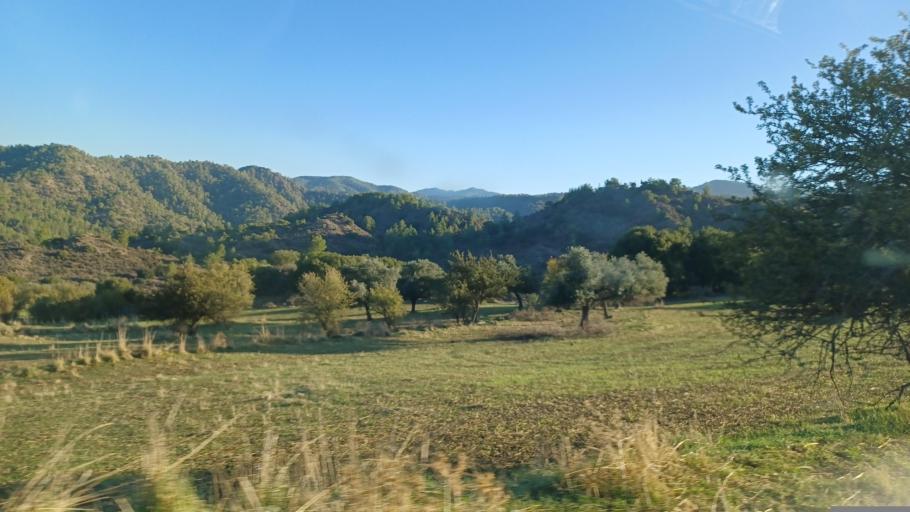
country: CY
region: Pafos
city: Polis
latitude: 34.9484
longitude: 32.5574
